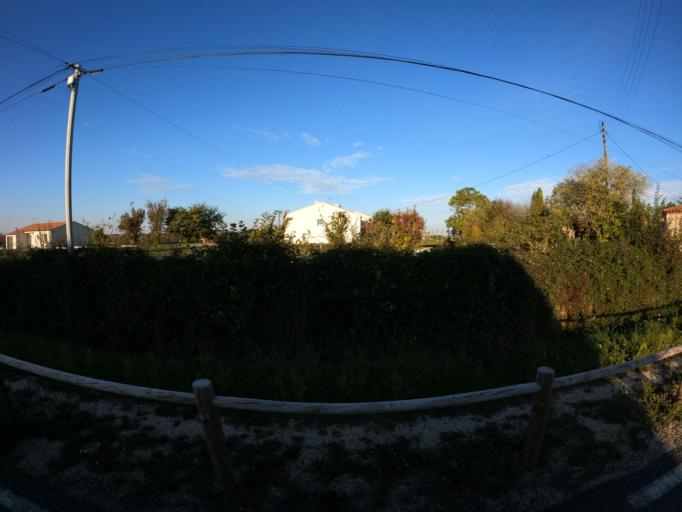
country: FR
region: Pays de la Loire
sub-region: Departement de la Vendee
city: Sainte-Hermine
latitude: 46.5516
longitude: -1.0447
